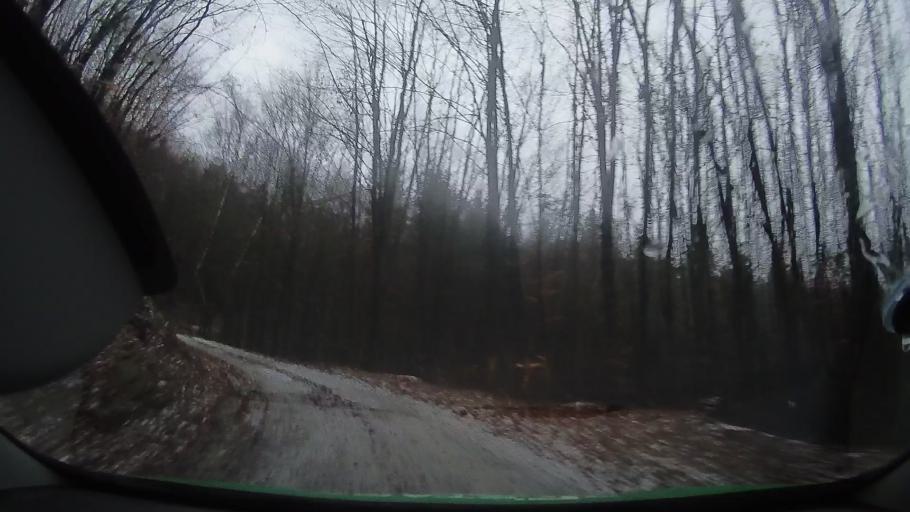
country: RO
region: Alba
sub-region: Comuna Avram Iancu
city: Avram Iancu
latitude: 46.3105
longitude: 22.7961
